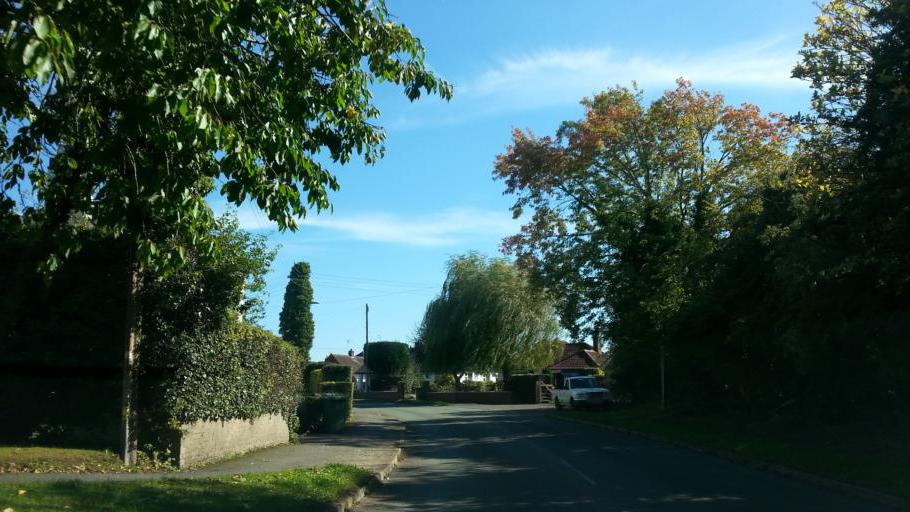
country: GB
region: England
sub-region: Staffordshire
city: Stafford
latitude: 52.8011
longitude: -2.1660
